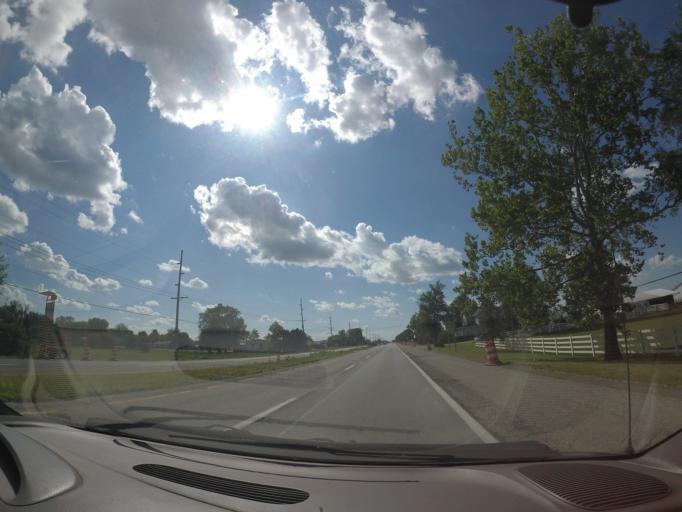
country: US
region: Ohio
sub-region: Sandusky County
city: Clyde
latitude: 41.3228
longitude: -83.0214
